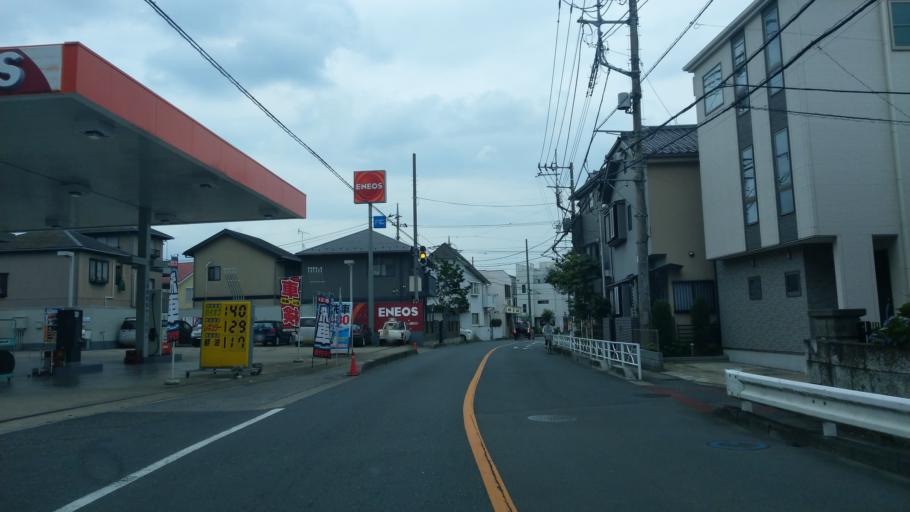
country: JP
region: Saitama
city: Shimotoda
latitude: 35.8575
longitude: 139.6935
